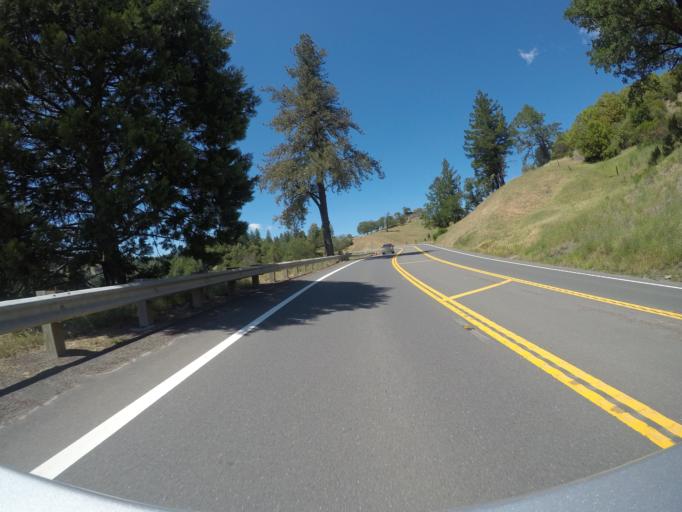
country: US
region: California
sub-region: Mendocino County
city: Laytonville
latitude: 39.7692
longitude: -123.5454
